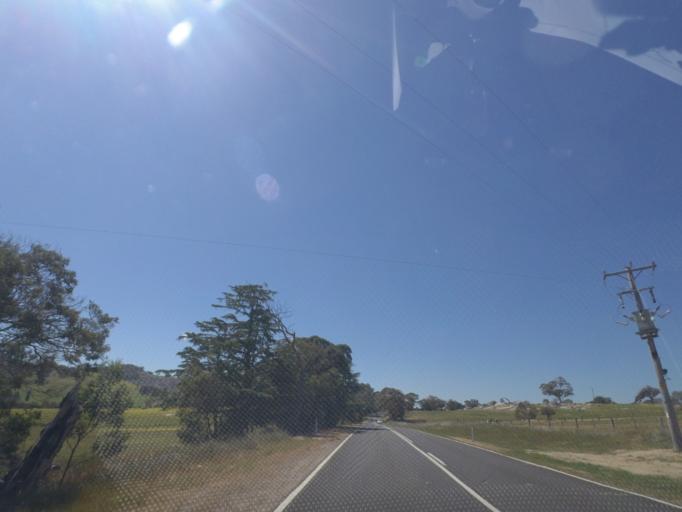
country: AU
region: Victoria
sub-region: Hume
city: Sunbury
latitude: -37.0757
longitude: 144.7705
